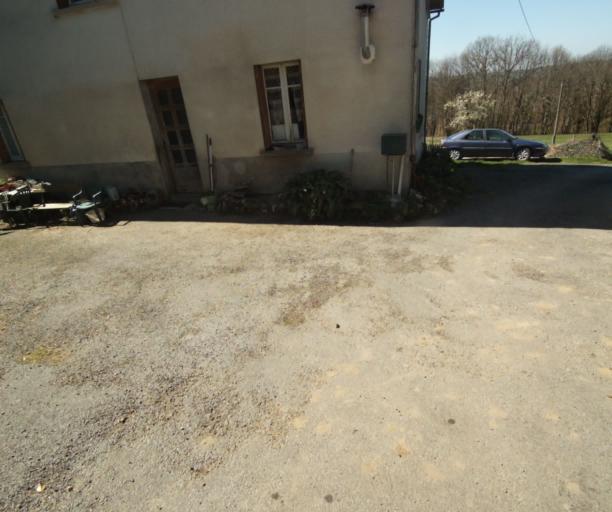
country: FR
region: Limousin
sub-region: Departement de la Correze
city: Saint-Mexant
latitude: 45.2890
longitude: 1.6368
